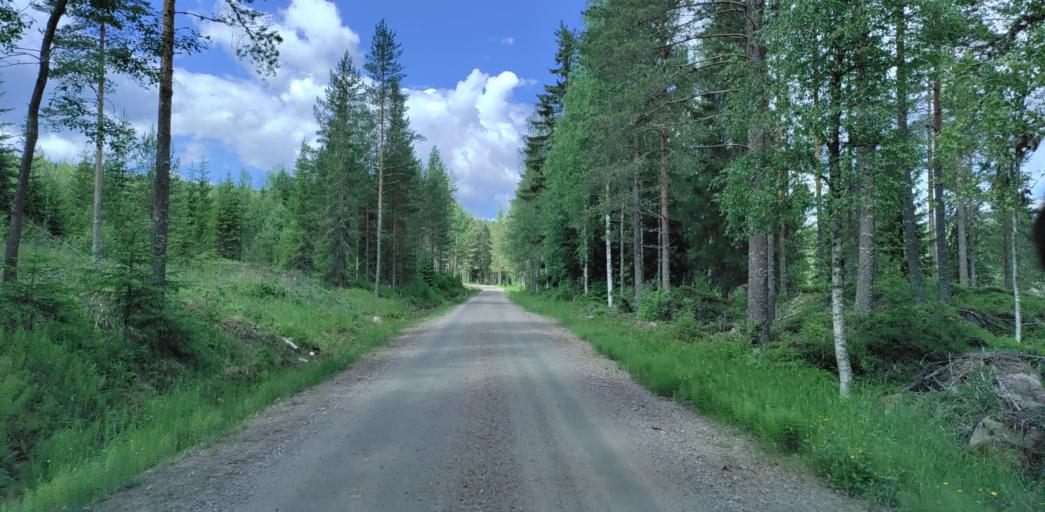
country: SE
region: Vaermland
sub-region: Hagfors Kommun
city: Ekshaerad
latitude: 60.1024
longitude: 13.3596
